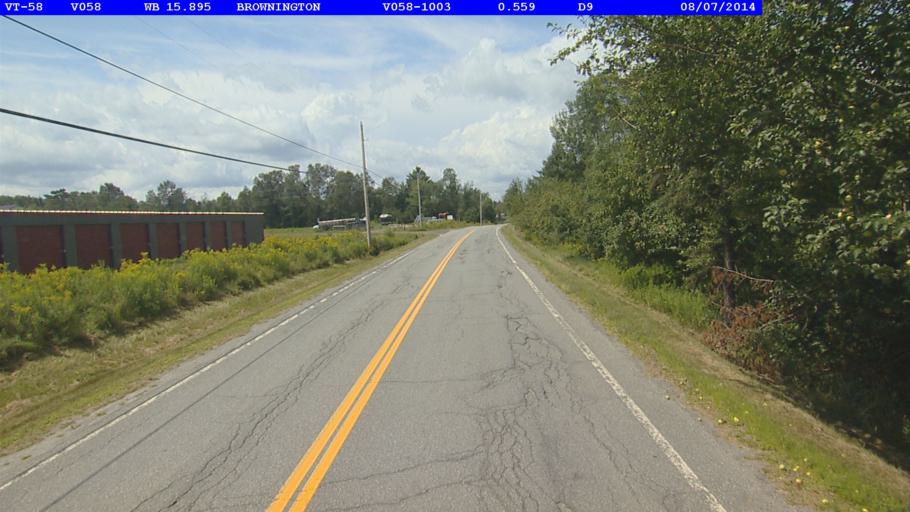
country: US
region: Vermont
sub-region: Orleans County
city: Newport
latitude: 44.8035
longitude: -72.1343
